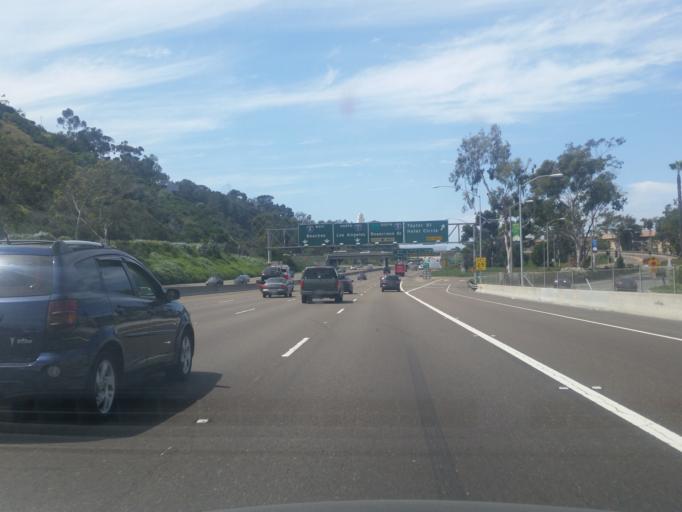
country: US
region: California
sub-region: San Diego County
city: San Diego
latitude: 32.7596
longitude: -117.1849
